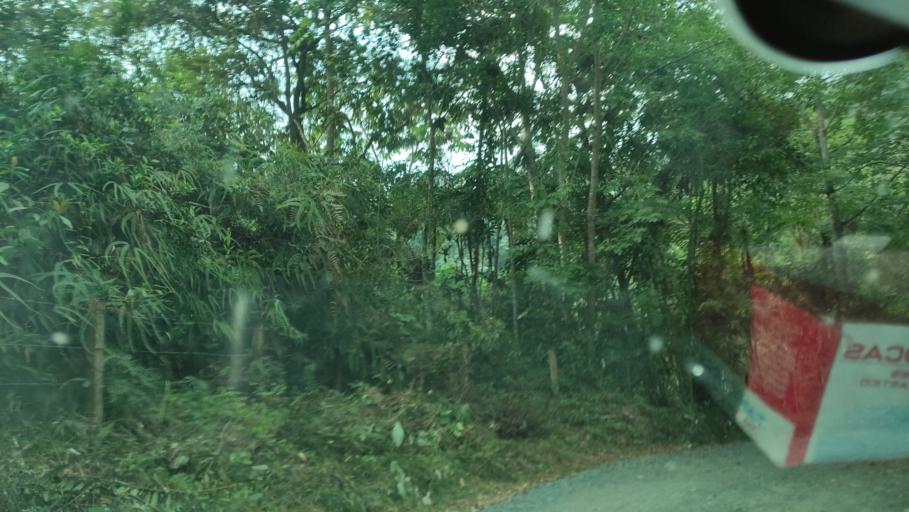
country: CO
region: Valle del Cauca
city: San Pedro
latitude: 3.8798
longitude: -76.1535
